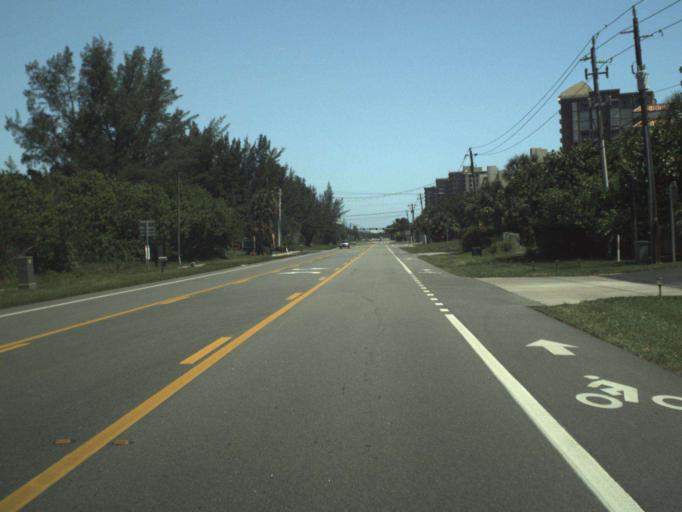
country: US
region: Florida
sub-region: Saint Lucie County
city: Fort Pierce North
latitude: 27.5072
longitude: -80.3055
